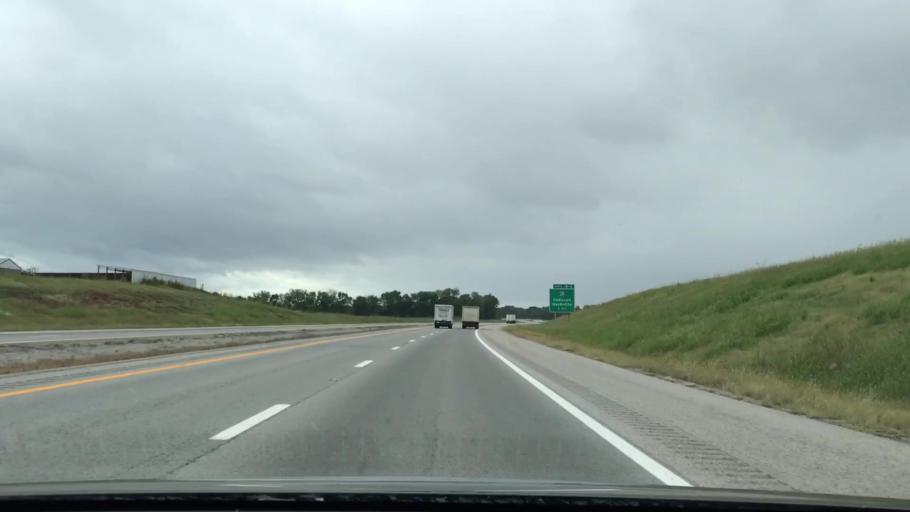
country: US
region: Kentucky
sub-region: Christian County
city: Hopkinsville
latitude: 36.7630
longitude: -87.5015
